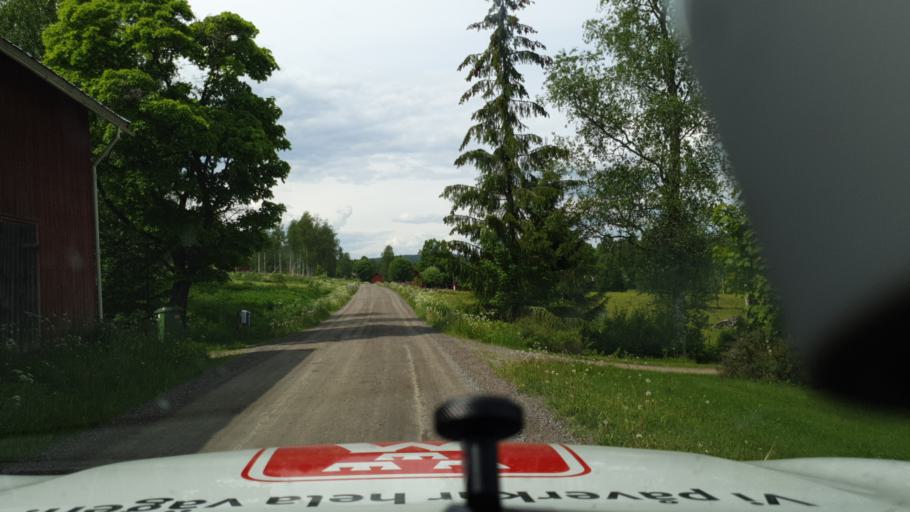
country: SE
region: Vaermland
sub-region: Torsby Kommun
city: Torsby
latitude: 59.9681
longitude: 12.8738
